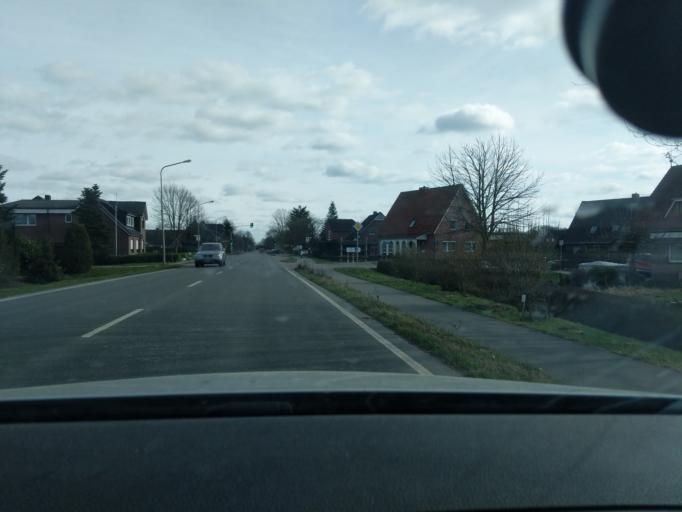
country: DE
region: Lower Saxony
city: Drochtersen
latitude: 53.7004
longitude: 9.4096
